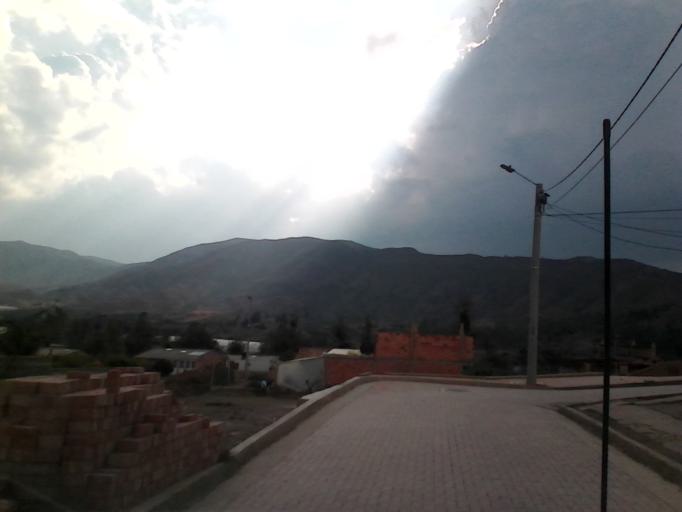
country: CO
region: Boyaca
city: Sachica
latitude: 5.5870
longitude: -73.5449
